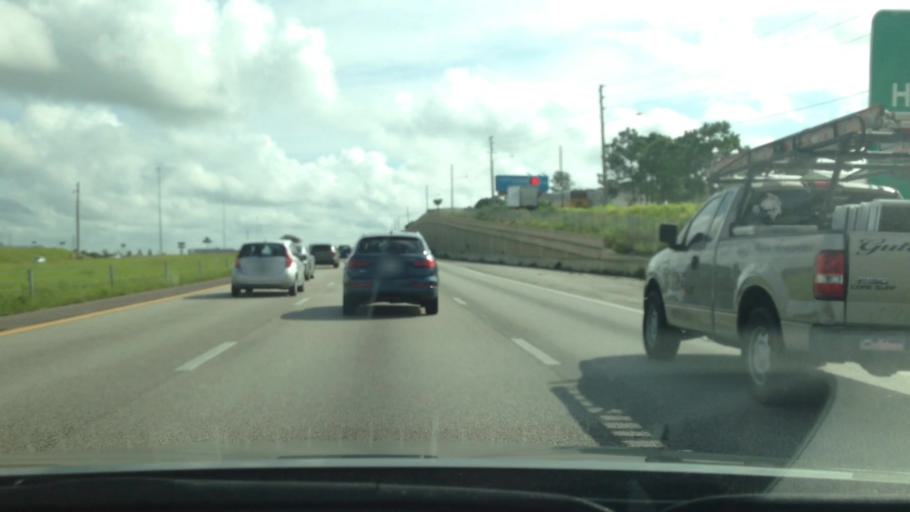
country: US
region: Florida
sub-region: Polk County
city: Davenport
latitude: 28.2265
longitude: -81.6571
